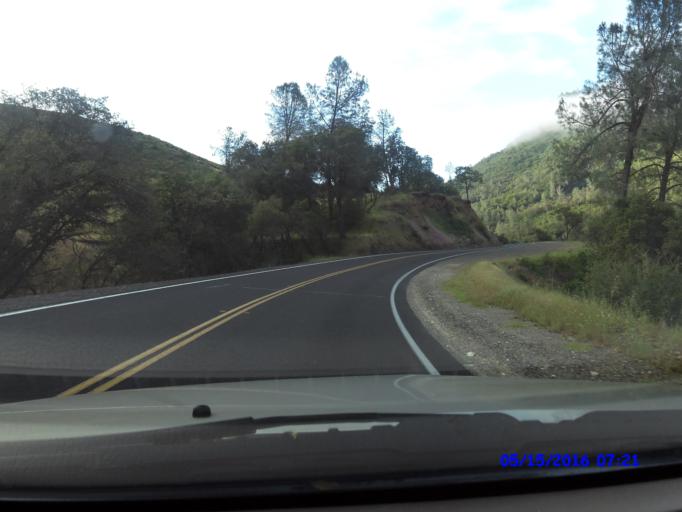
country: US
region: California
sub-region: Tuolumne County
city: Tuolumne City
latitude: 37.7833
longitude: -120.2736
